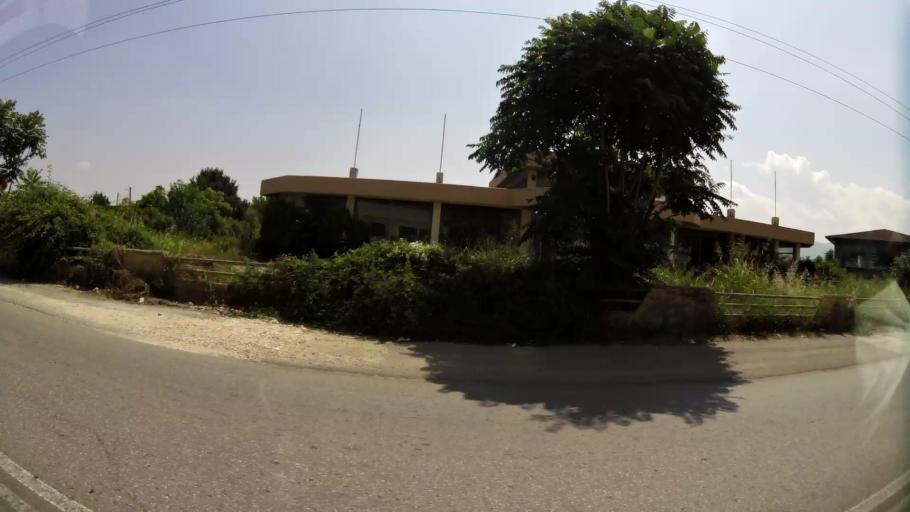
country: GR
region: Central Macedonia
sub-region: Nomos Imathias
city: Veroia
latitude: 40.5169
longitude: 22.2122
